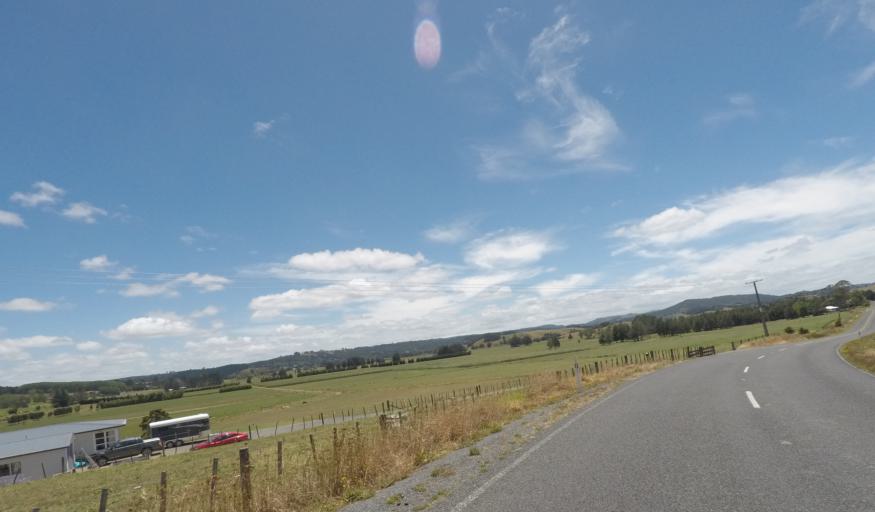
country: NZ
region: Northland
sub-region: Whangarei
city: Whangarei
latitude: -35.5585
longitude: 174.2920
